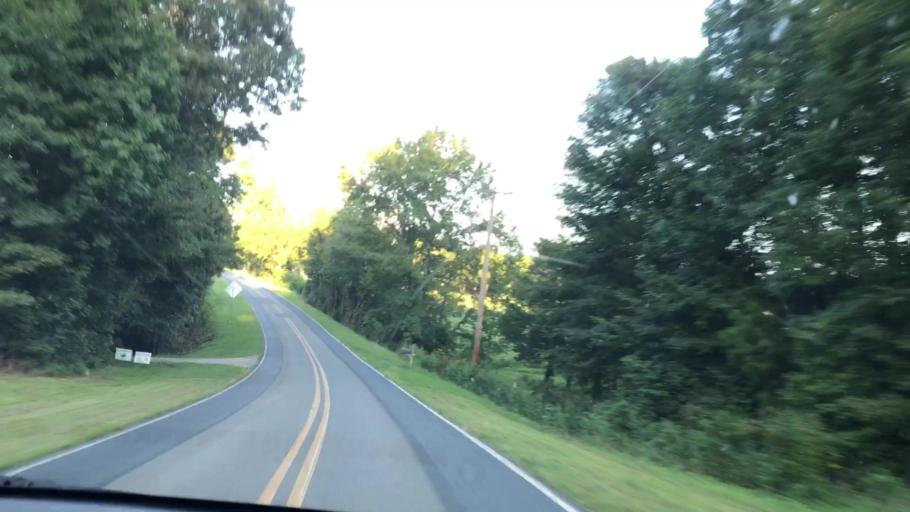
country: US
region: North Carolina
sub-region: Randolph County
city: Franklinville
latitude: 35.8015
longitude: -79.6791
